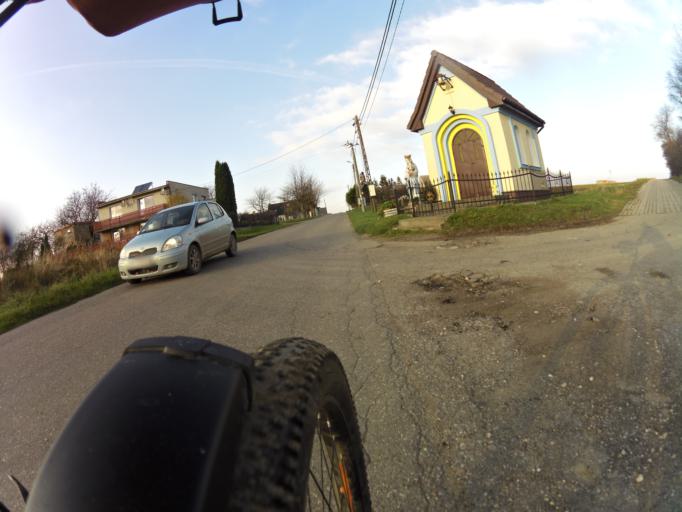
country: PL
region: Pomeranian Voivodeship
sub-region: Powiat pucki
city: Krokowa
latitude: 54.7623
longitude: 18.1820
